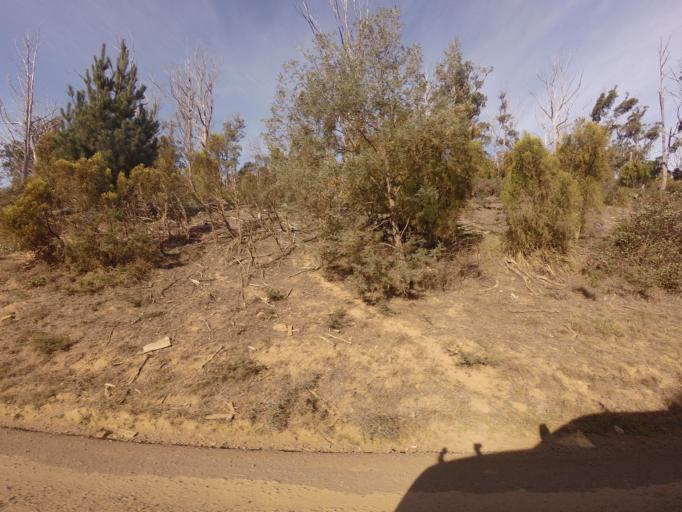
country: AU
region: Tasmania
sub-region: Sorell
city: Sorell
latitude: -42.4893
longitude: 147.4337
